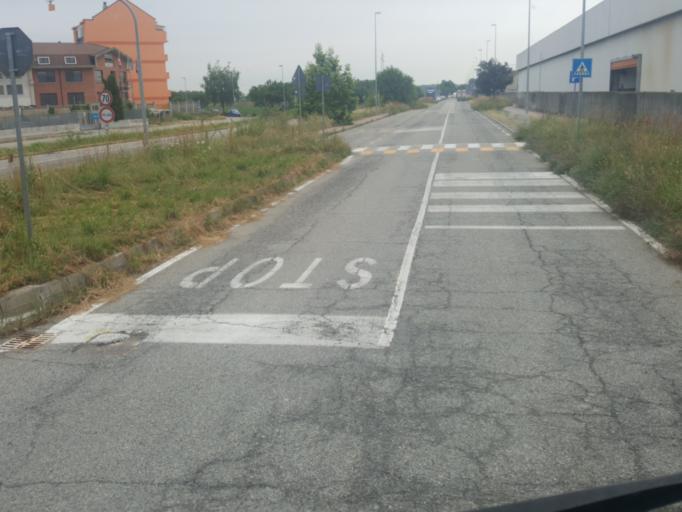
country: IT
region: Piedmont
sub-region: Provincia di Torino
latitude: 44.9450
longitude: 7.5445
